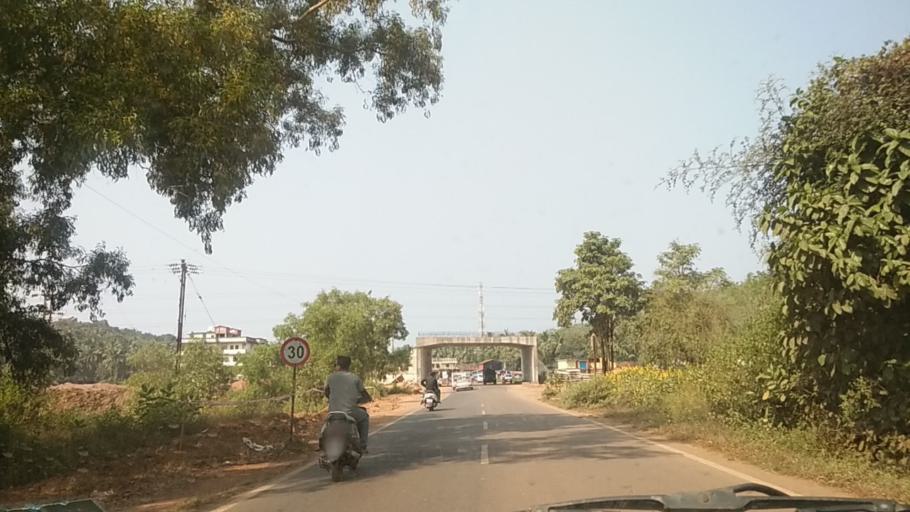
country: IN
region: Goa
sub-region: South Goa
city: Kankon
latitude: 15.0106
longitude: 74.0383
